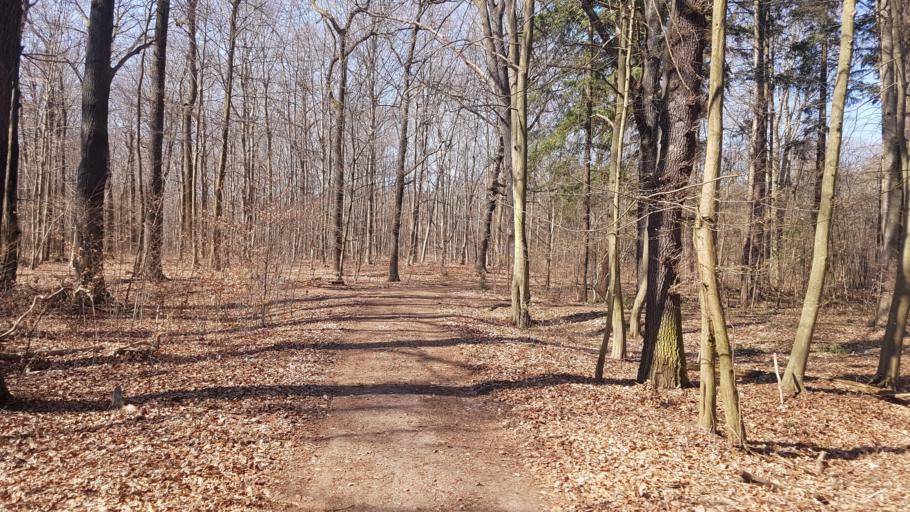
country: DE
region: Brandenburg
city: Crinitz
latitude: 51.7487
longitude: 13.7951
